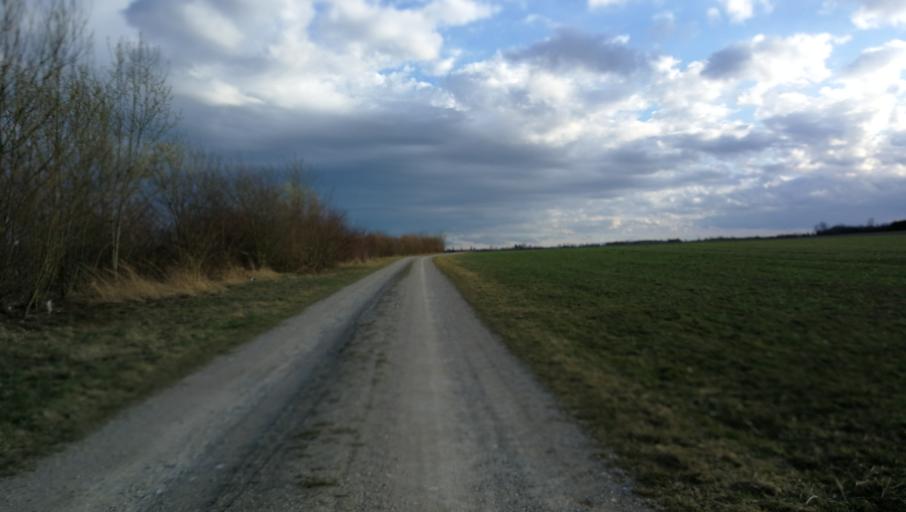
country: DE
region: Bavaria
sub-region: Upper Bavaria
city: Fuerstenfeldbruck
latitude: 48.2085
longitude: 11.2151
